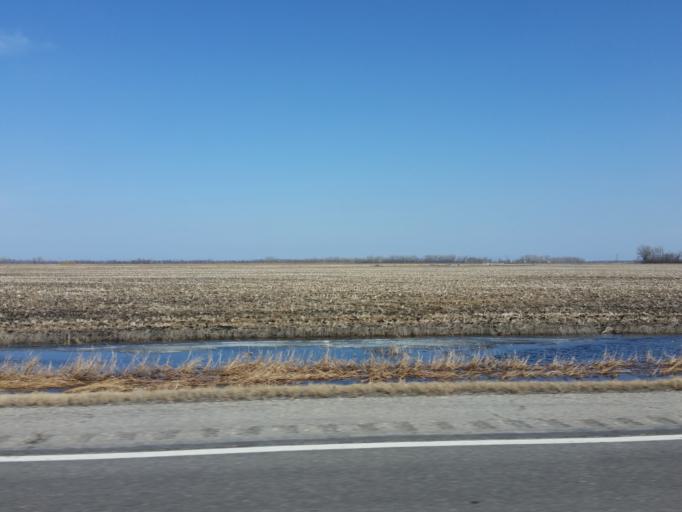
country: US
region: North Dakota
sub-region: Grand Forks County
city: Grand Forks Air Force Base
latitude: 48.1627
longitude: -97.2862
